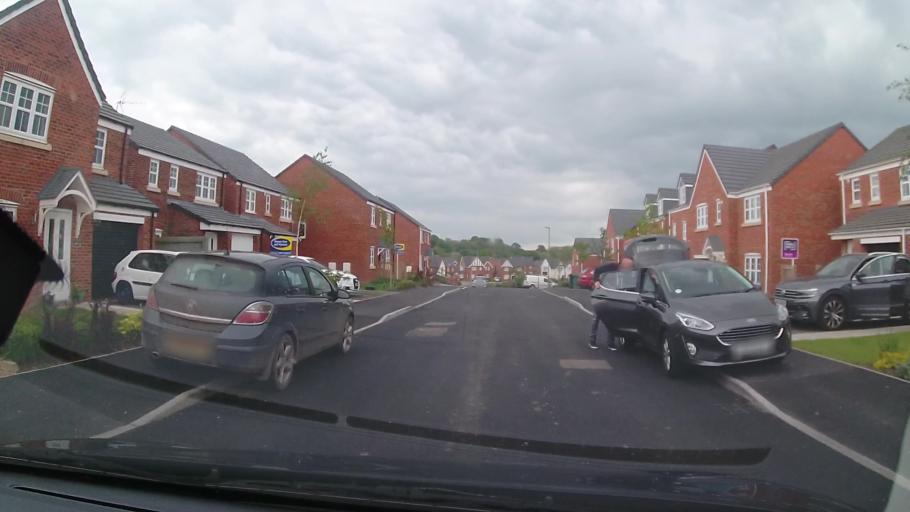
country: GB
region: England
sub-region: Shropshire
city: Ellesmere
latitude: 52.9032
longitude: -2.8985
